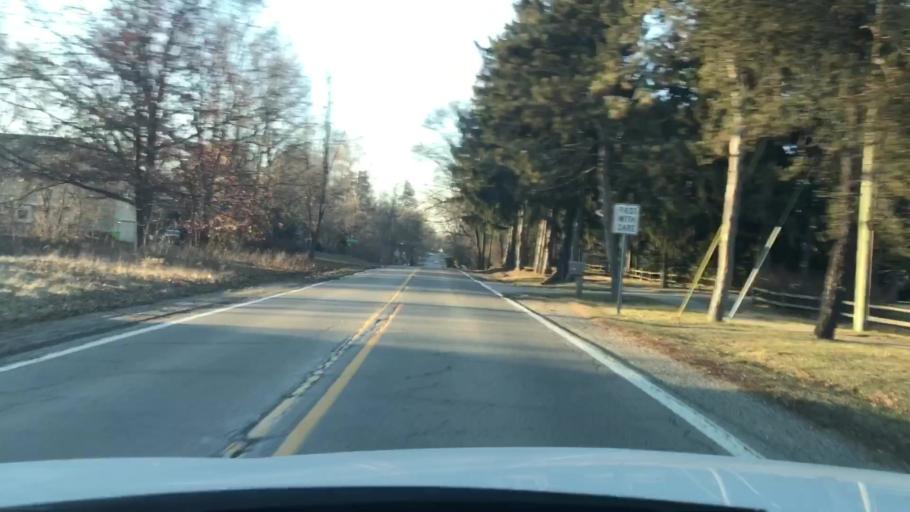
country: US
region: Michigan
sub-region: Oakland County
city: West Bloomfield Township
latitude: 42.5965
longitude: -83.4033
